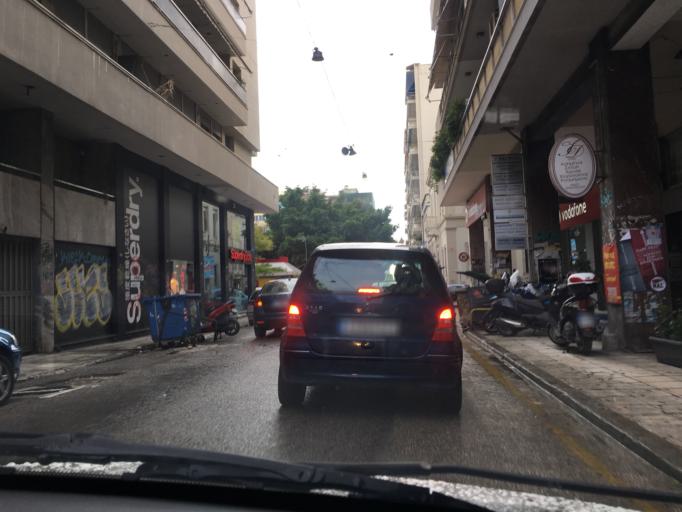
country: GR
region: West Greece
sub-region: Nomos Achaias
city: Patra
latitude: 38.2500
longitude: 21.7379
